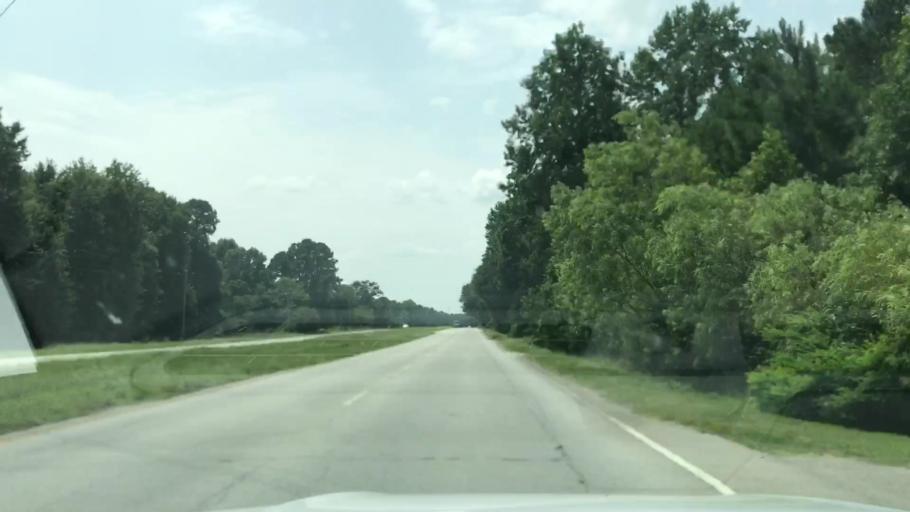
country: US
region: South Carolina
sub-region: Charleston County
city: Awendaw
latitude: 33.0509
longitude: -79.5569
